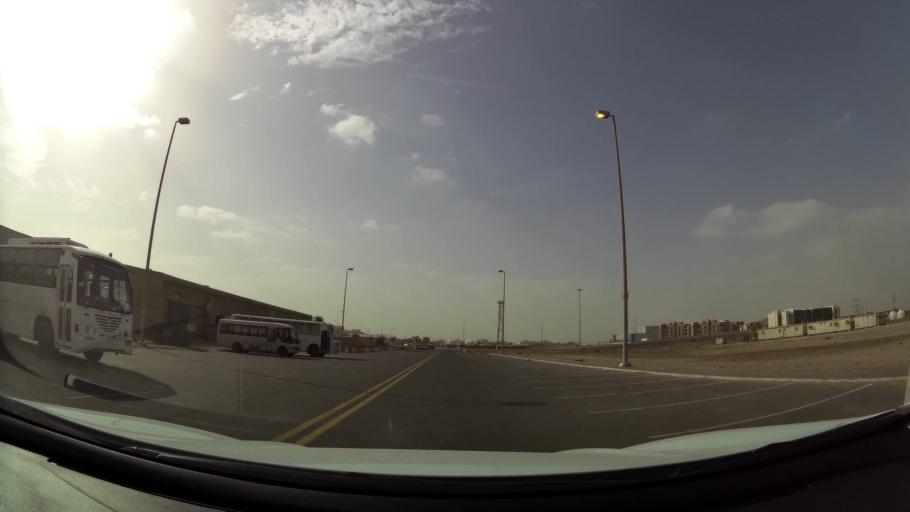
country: AE
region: Abu Dhabi
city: Abu Dhabi
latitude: 24.4105
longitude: 54.5167
